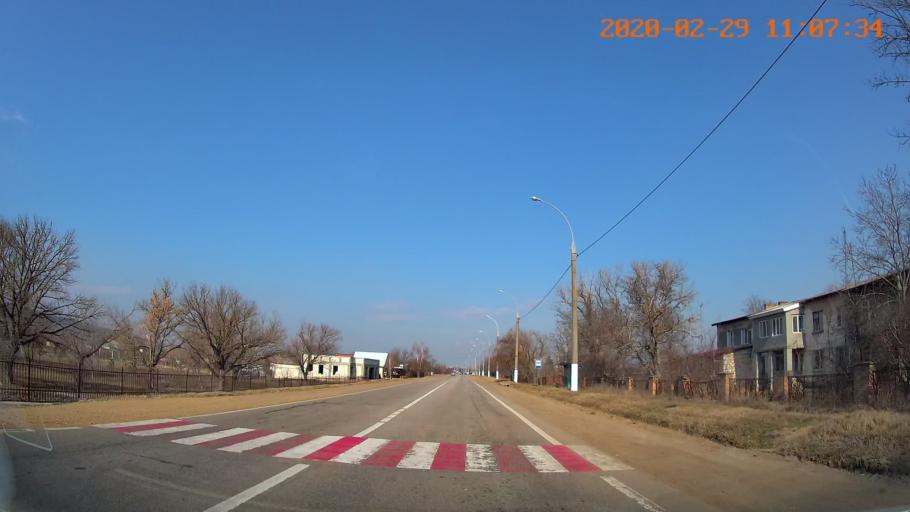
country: MD
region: Criuleni
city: Criuleni
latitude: 47.2264
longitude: 29.1812
